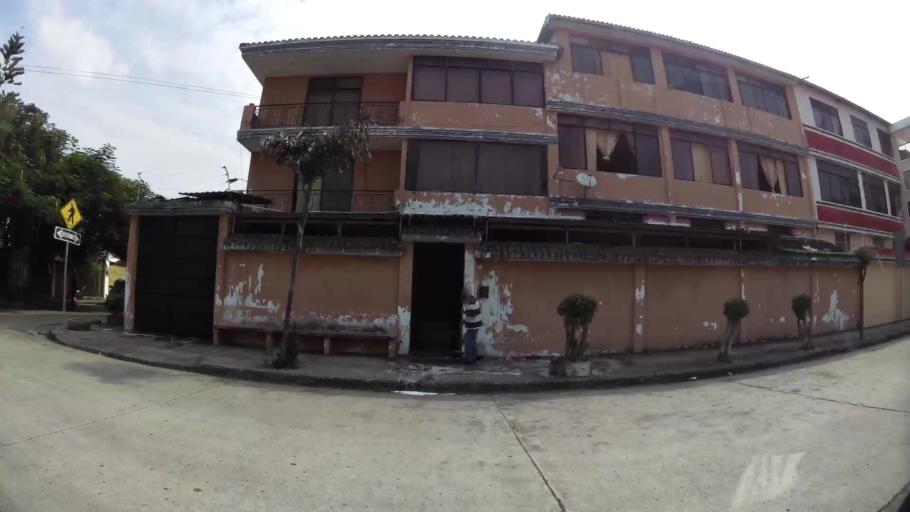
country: EC
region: Guayas
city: Guayaquil
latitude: -2.2434
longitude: -79.8989
